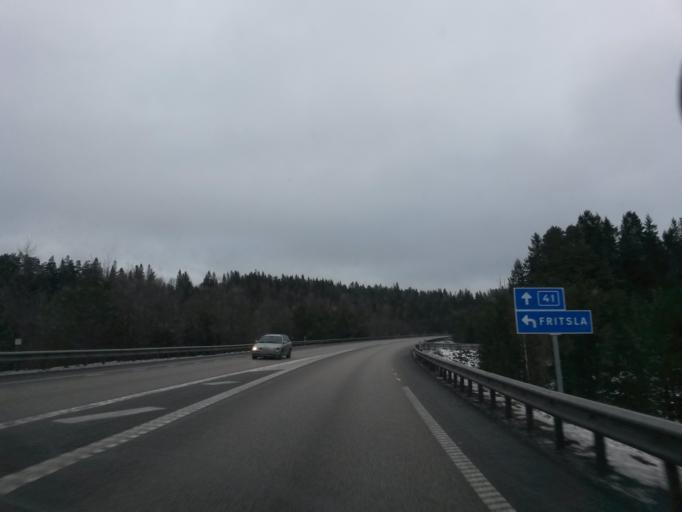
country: SE
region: Vaestra Goetaland
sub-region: Marks Kommun
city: Fritsla
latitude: 57.5694
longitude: 12.8358
